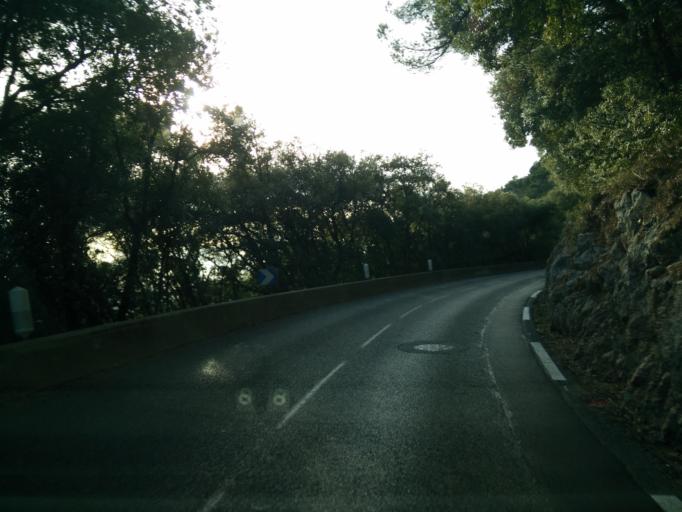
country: FR
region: Provence-Alpes-Cote d'Azur
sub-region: Departement des Alpes-Maritimes
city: Le Tignet
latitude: 43.6358
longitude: 6.8357
